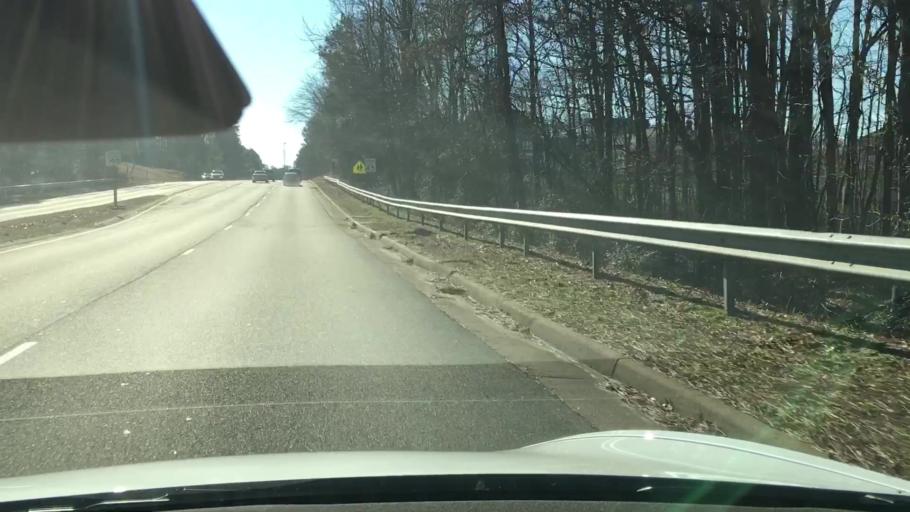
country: US
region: Virginia
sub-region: Henrico County
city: Tuckahoe
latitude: 37.5873
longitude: -77.5721
